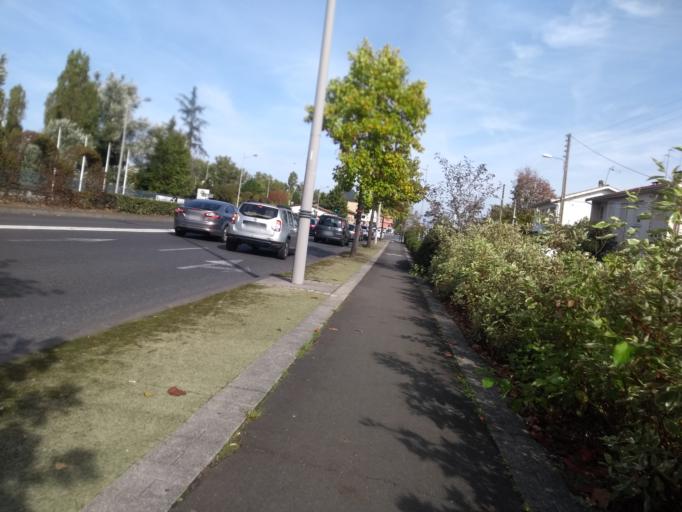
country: FR
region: Aquitaine
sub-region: Departement de la Gironde
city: Talence
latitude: 44.7921
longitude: -0.6052
